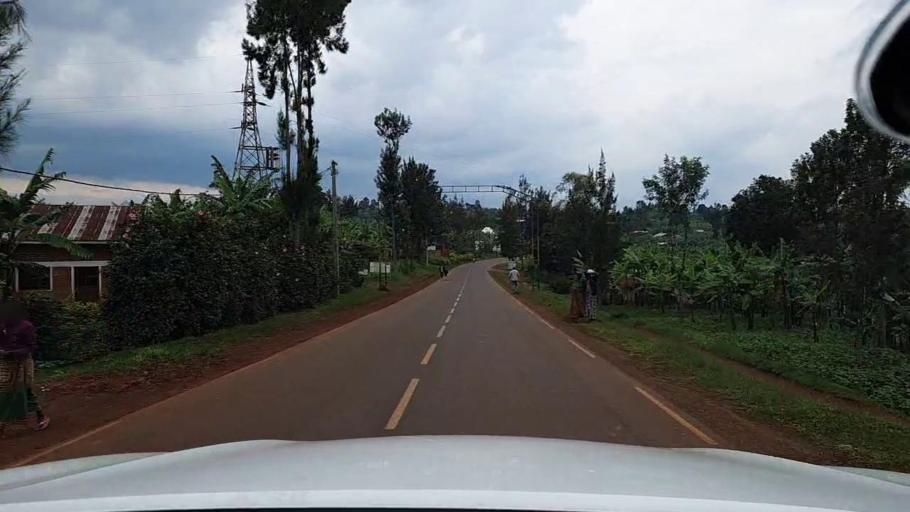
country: RW
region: Western Province
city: Cyangugu
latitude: -2.6136
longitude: 28.9415
